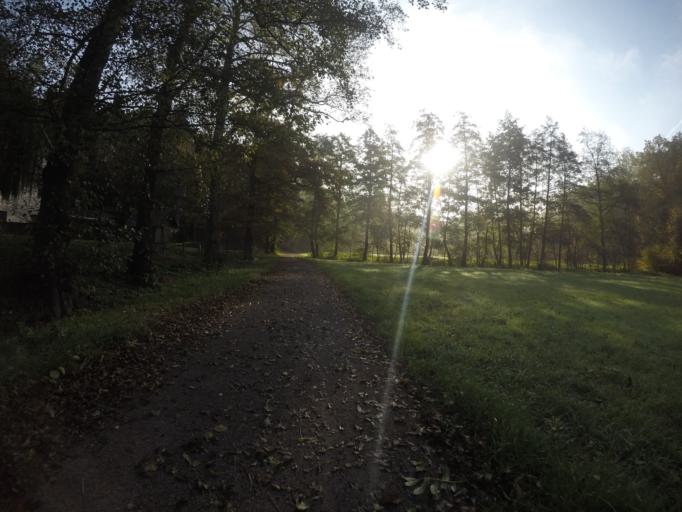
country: DE
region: Baden-Wuerttemberg
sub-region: Regierungsbezirk Stuttgart
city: Leinfelden-Echterdingen
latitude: 48.7125
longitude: 9.1808
